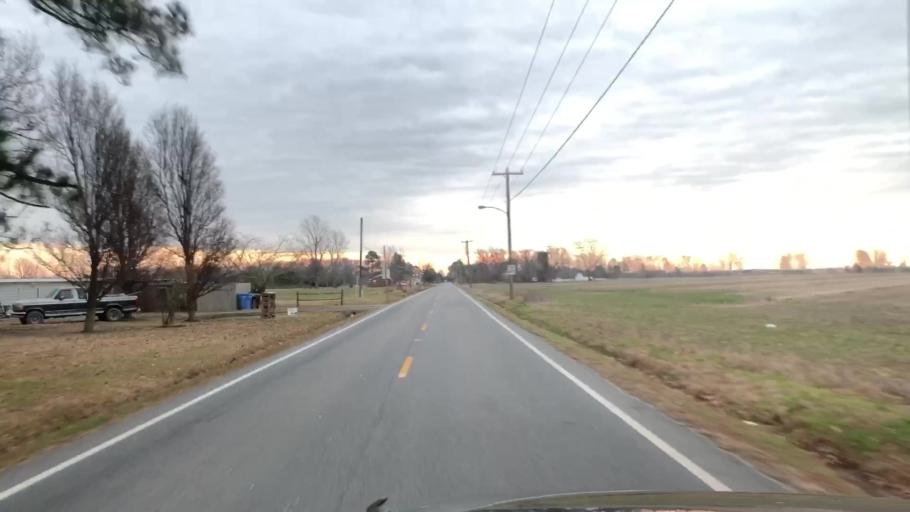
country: US
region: North Carolina
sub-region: Currituck County
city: Moyock
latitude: 36.6279
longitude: -76.1685
